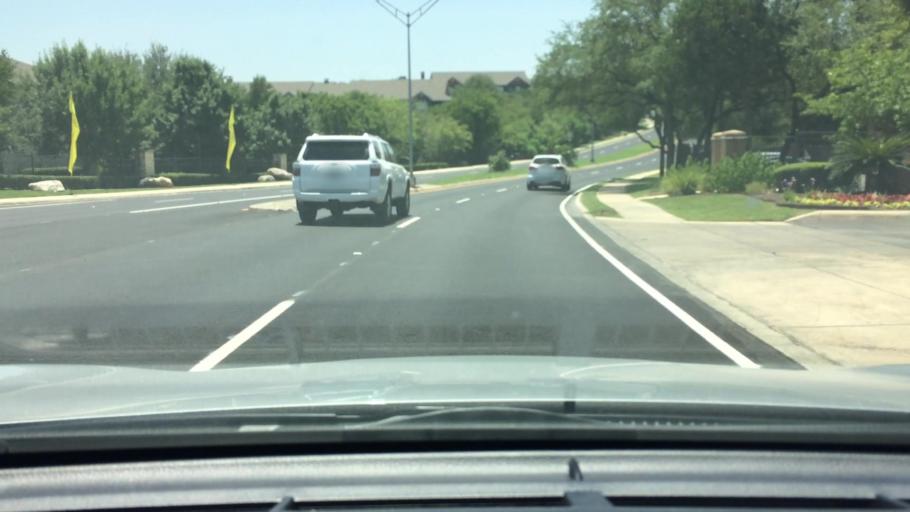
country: US
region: Texas
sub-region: Bexar County
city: Shavano Park
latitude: 29.5576
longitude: -98.5746
